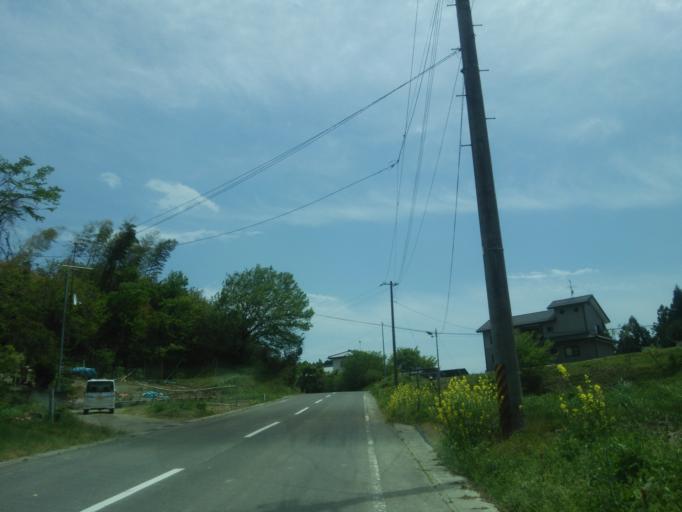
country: JP
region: Fukushima
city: Nihommatsu
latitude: 37.5996
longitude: 140.4231
